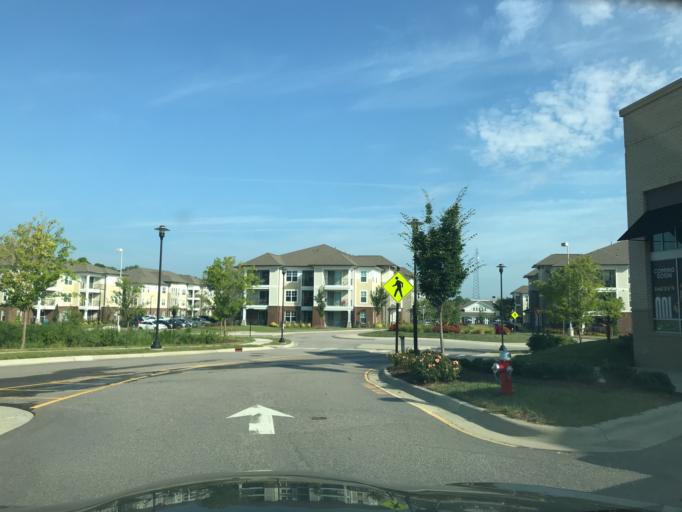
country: US
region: North Carolina
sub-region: Wake County
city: Green Level
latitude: 35.8489
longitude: -78.8912
